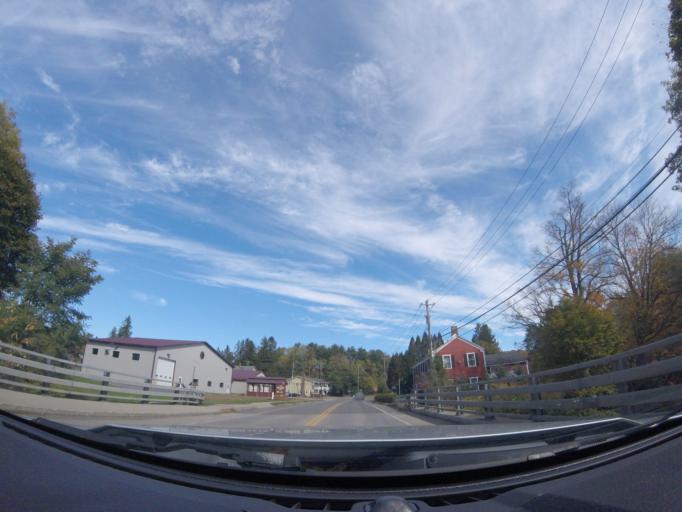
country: US
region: New York
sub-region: Tompkins County
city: Dryden
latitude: 42.5514
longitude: -76.2920
